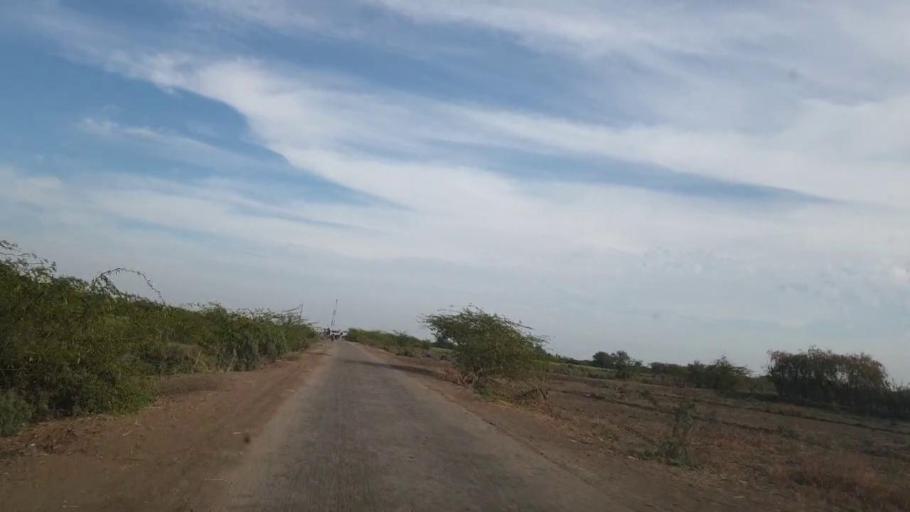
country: PK
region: Sindh
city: Pithoro
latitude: 25.6293
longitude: 69.4107
